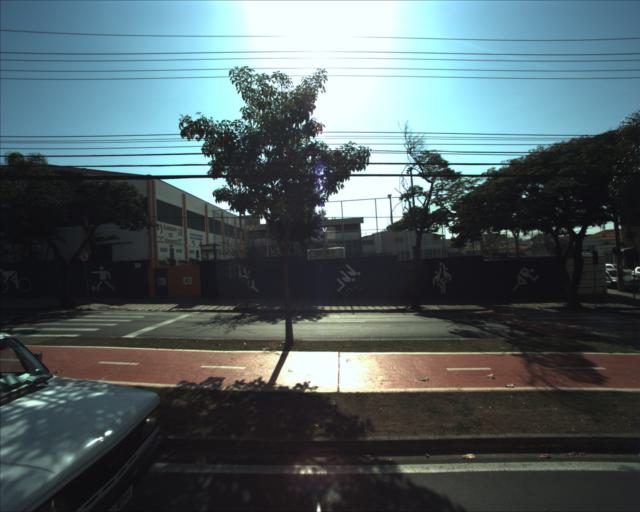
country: BR
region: Sao Paulo
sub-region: Sorocaba
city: Sorocaba
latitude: -23.4944
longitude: -47.4649
